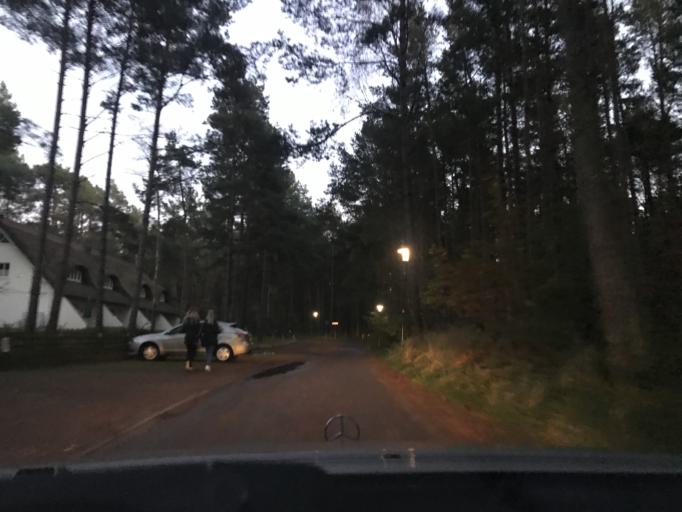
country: DE
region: Mecklenburg-Vorpommern
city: Karlshagen
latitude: 54.1126
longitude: 13.8516
